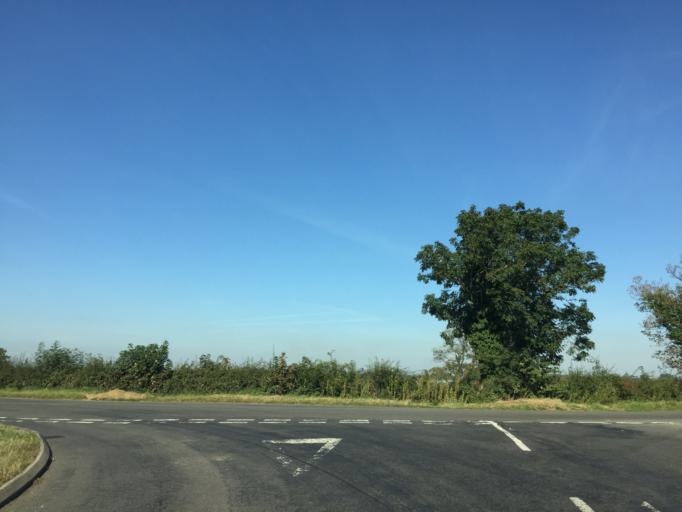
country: GB
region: England
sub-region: Leicestershire
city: Asfordby
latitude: 52.6757
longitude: -0.9382
